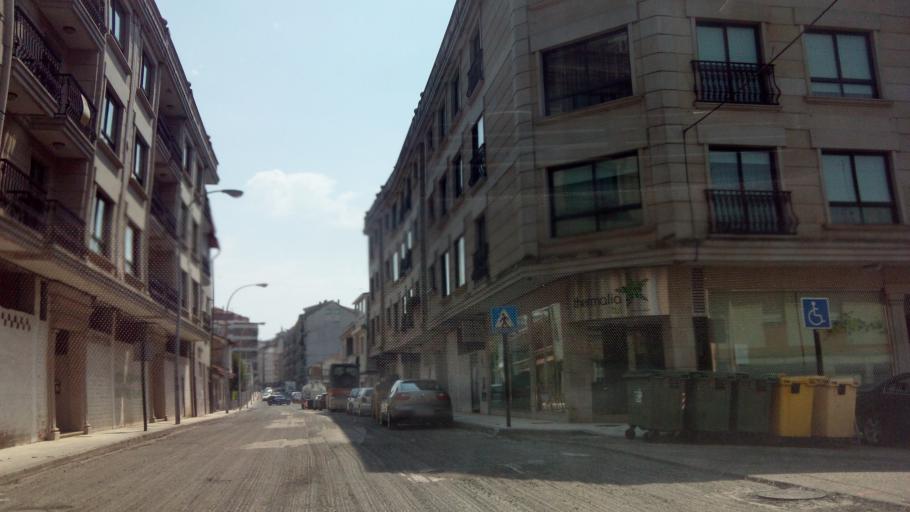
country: ES
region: Galicia
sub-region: Provincia de Pontevedra
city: Tui
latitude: 42.0513
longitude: -8.6499
